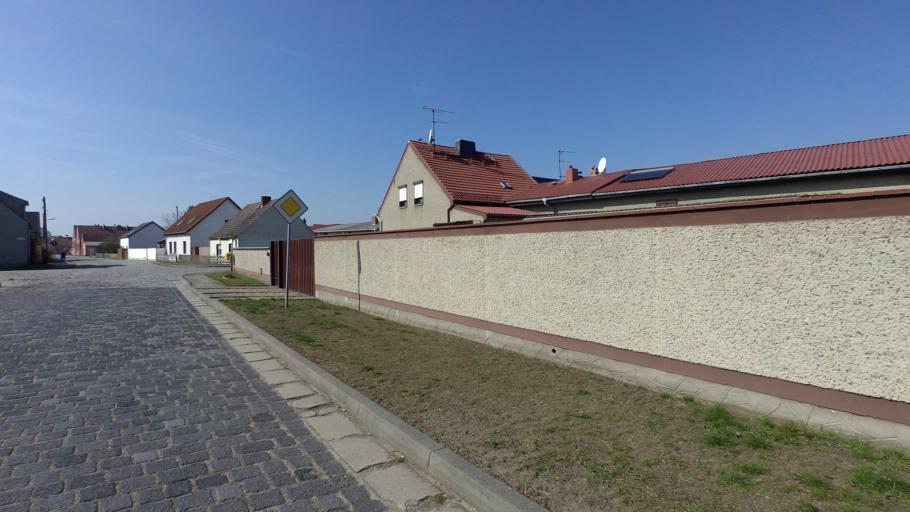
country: DE
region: Brandenburg
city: Baruth
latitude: 52.0766
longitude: 13.4884
